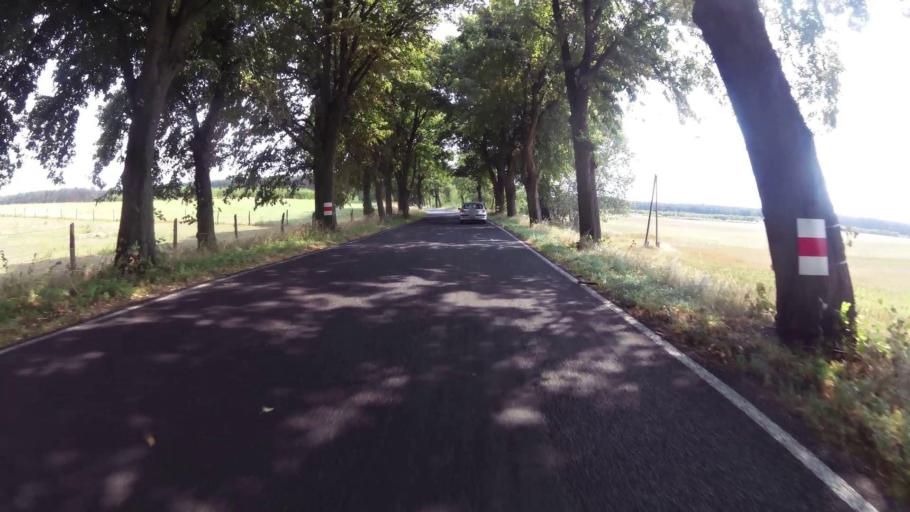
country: PL
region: West Pomeranian Voivodeship
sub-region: Powiat gryfinski
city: Moryn
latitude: 52.8396
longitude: 14.4050
